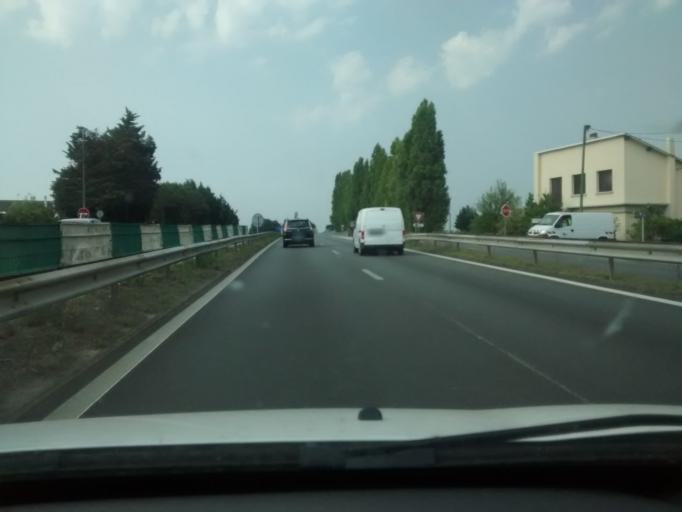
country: FR
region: Pays de la Loire
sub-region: Departement de la Loire-Atlantique
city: Trignac
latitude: 47.3194
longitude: -2.1931
